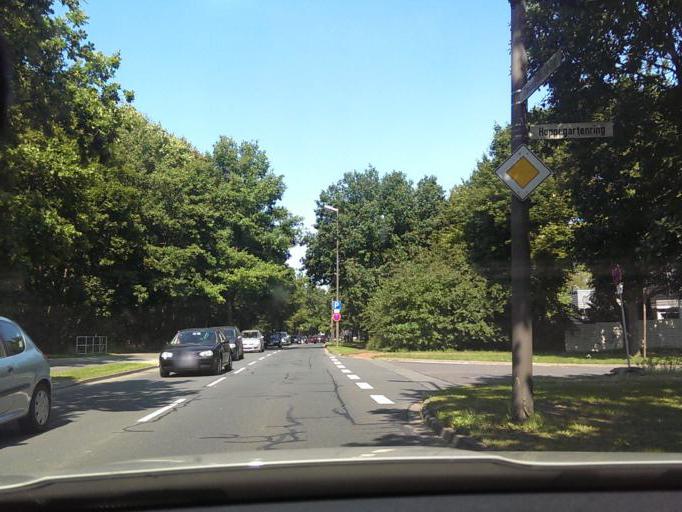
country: DE
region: Lower Saxony
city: Langenhagen
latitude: 52.4441
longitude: 9.7537
